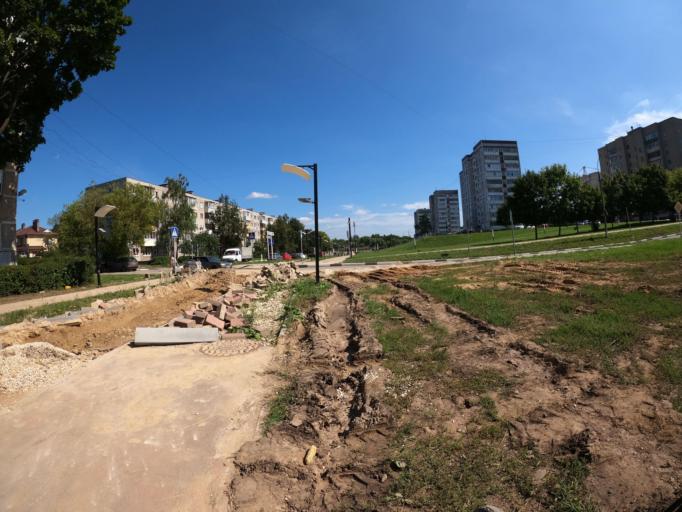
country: RU
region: Moskovskaya
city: Stupino
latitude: 54.8914
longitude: 38.0877
